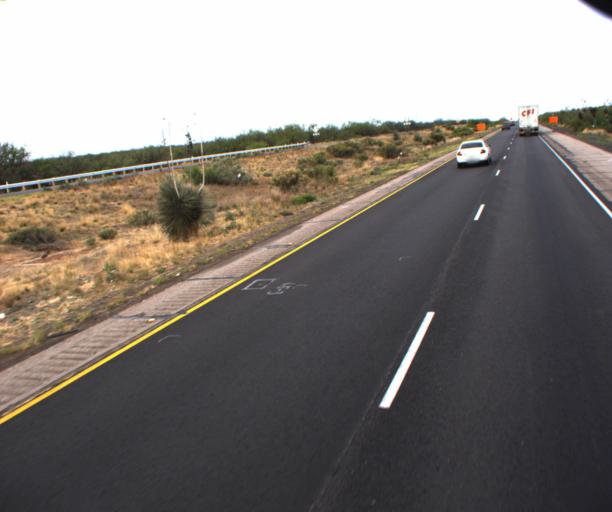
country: US
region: Arizona
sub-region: Cochise County
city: Whetstone
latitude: 31.9633
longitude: -110.3796
